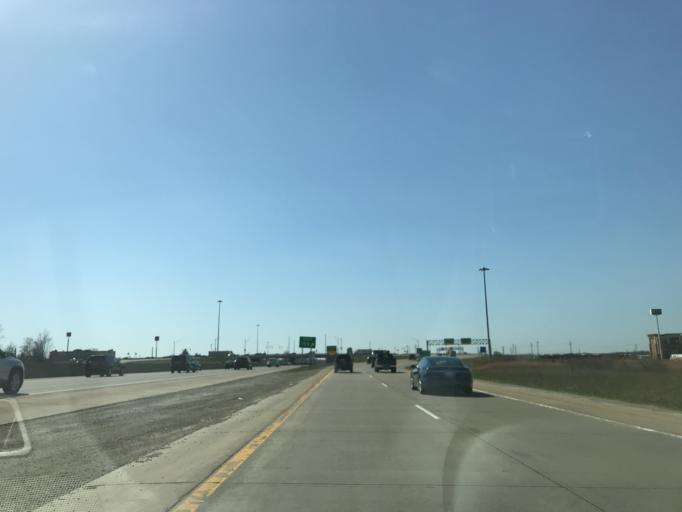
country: US
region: Michigan
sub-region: Oakland County
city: Wixom
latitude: 42.4972
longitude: -83.5304
